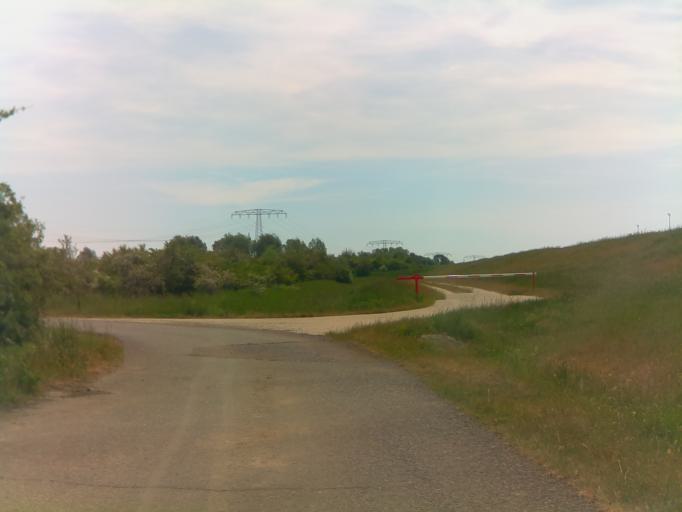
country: DE
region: Saxony-Anhalt
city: Glindenberg
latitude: 52.2141
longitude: 11.6824
